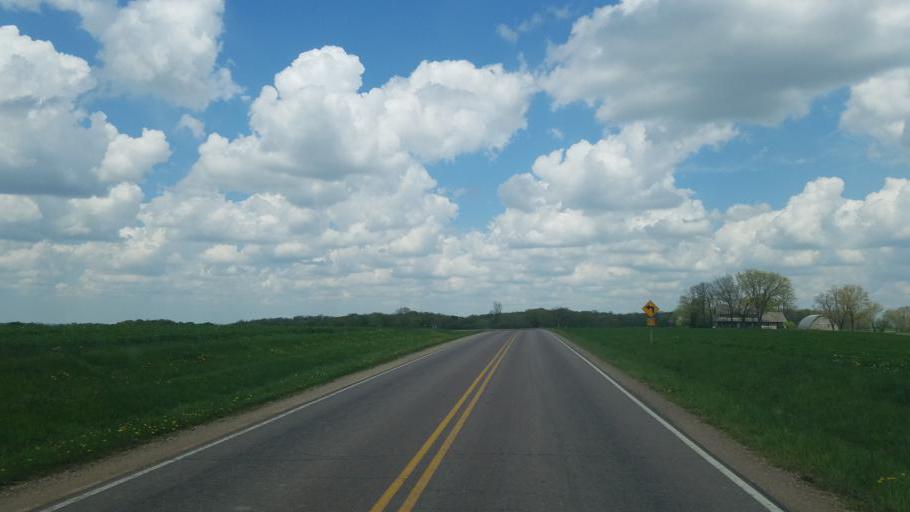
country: US
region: Wisconsin
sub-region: Vernon County
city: Hillsboro
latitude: 43.6026
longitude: -90.3223
